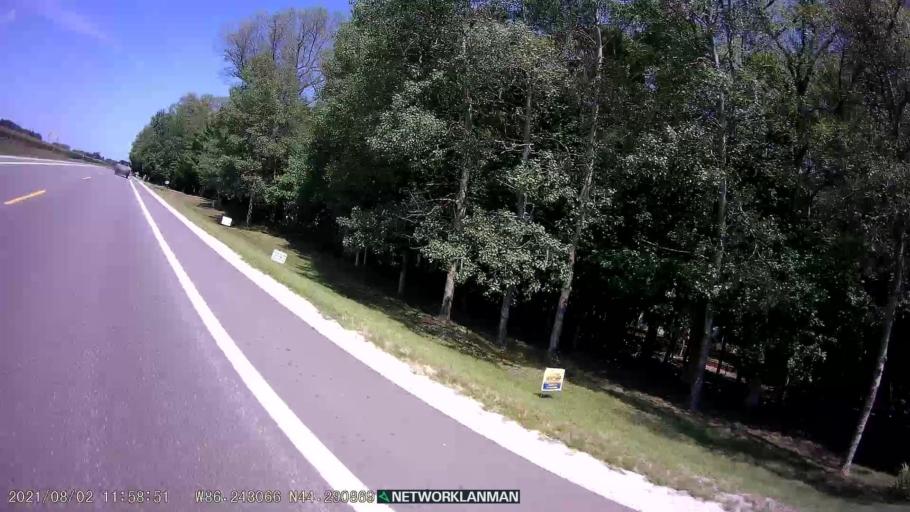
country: US
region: Michigan
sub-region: Manistee County
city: Manistee
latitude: 44.2908
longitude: -86.2430
